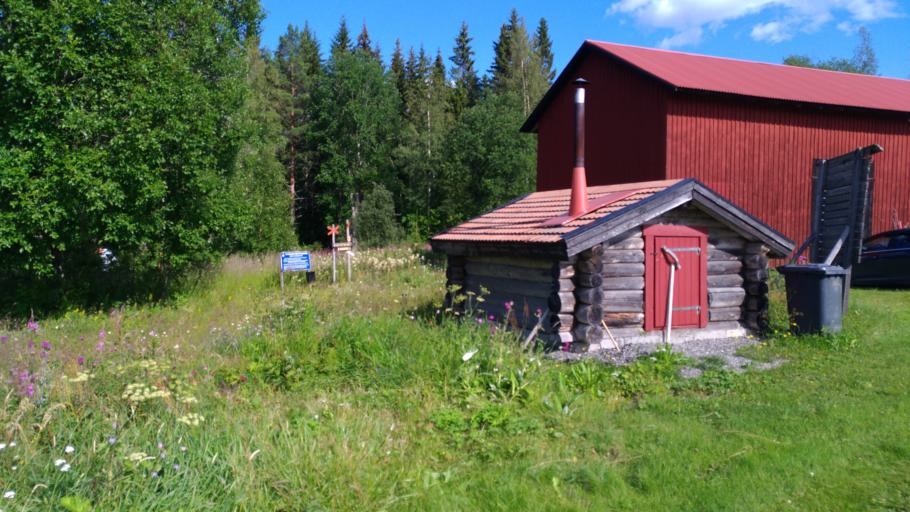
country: SE
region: Dalarna
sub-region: Gagnefs Kommun
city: Mockfjard
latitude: 60.3697
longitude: 15.0634
